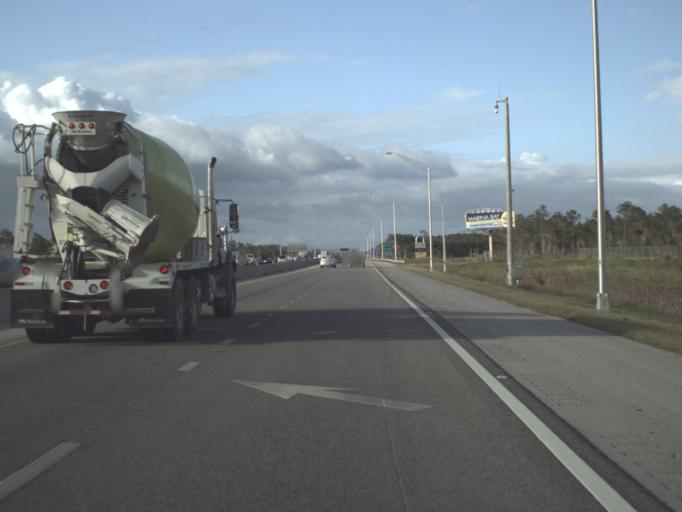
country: US
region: Florida
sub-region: Lee County
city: Three Oaks
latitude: 26.5222
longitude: -81.7944
